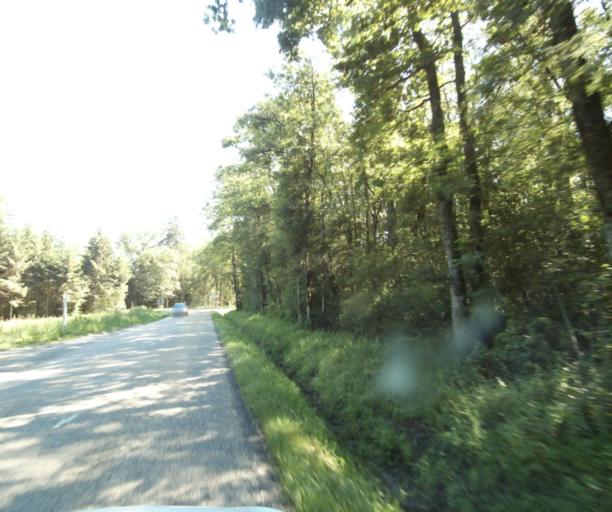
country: FR
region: Rhone-Alpes
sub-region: Departement de la Haute-Savoie
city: Ballaison
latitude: 46.2840
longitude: 6.3469
